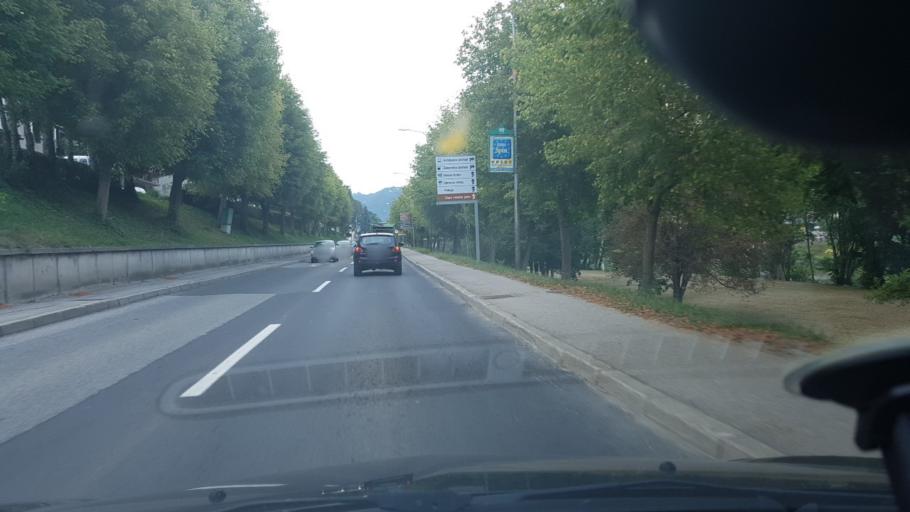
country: SI
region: Krsko
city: Krsko
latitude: 45.9538
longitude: 15.4865
